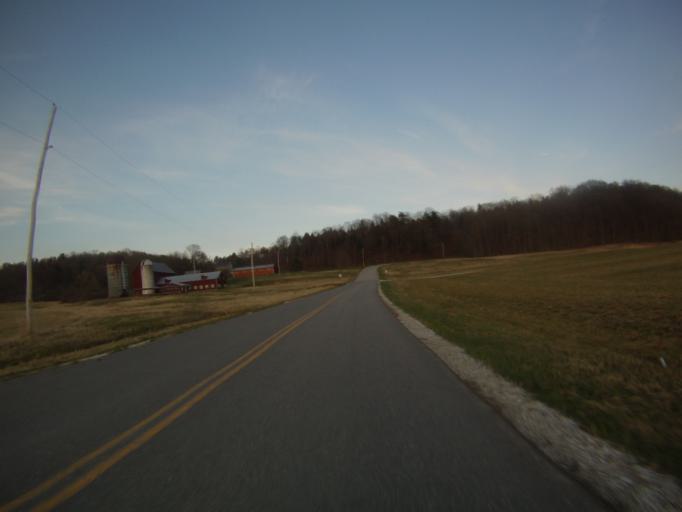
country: US
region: Vermont
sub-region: Addison County
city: Middlebury (village)
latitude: 44.0217
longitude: -73.2271
